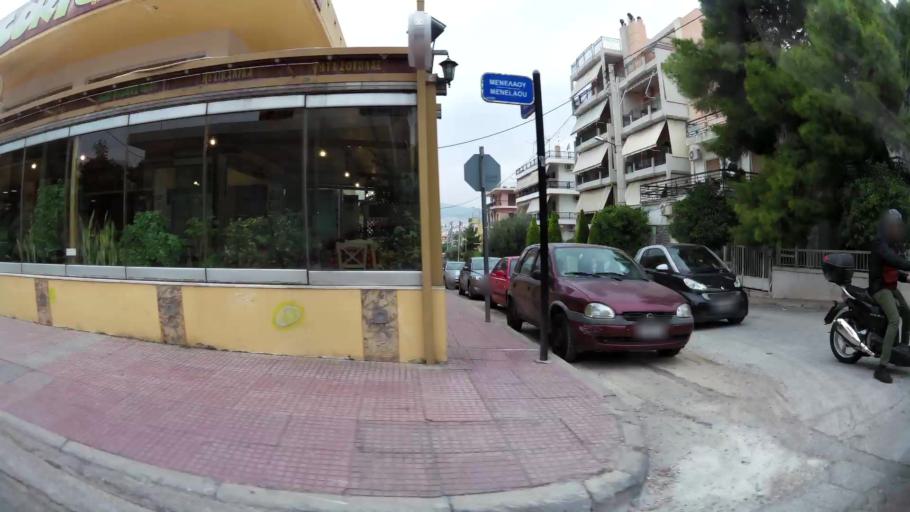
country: GR
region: Attica
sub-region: Nomarchia Athinas
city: Ilion
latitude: 38.0352
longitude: 23.7059
